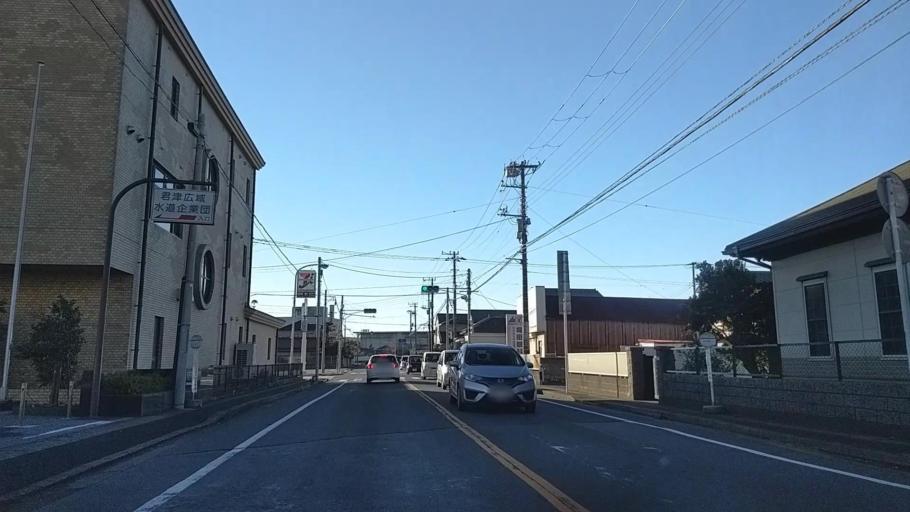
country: JP
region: Chiba
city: Kisarazu
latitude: 35.3781
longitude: 139.9186
